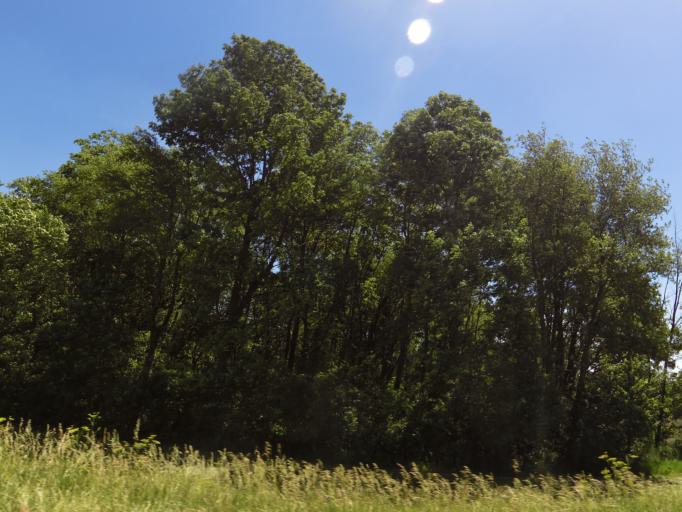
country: US
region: Illinois
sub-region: Vermilion County
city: Hoopeston
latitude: 40.4240
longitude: -87.6855
